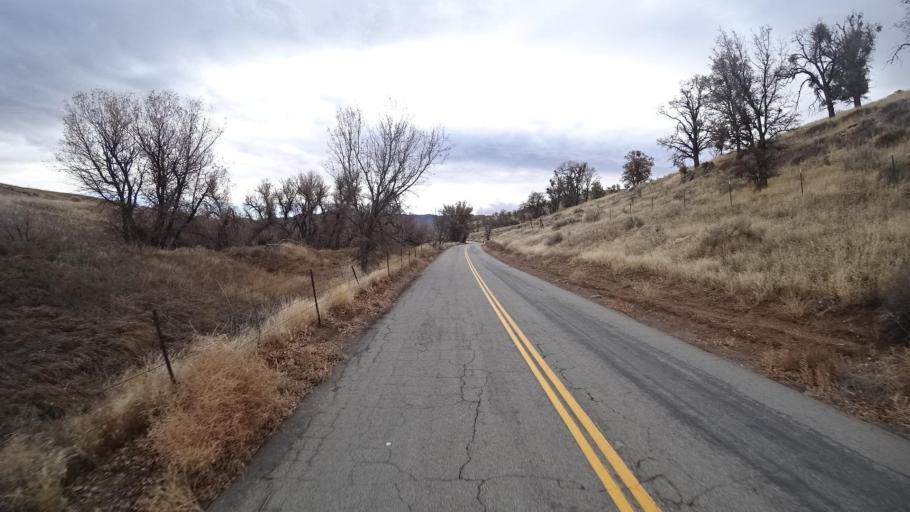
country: US
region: California
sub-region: Kern County
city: Golden Hills
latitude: 35.1258
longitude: -118.5546
